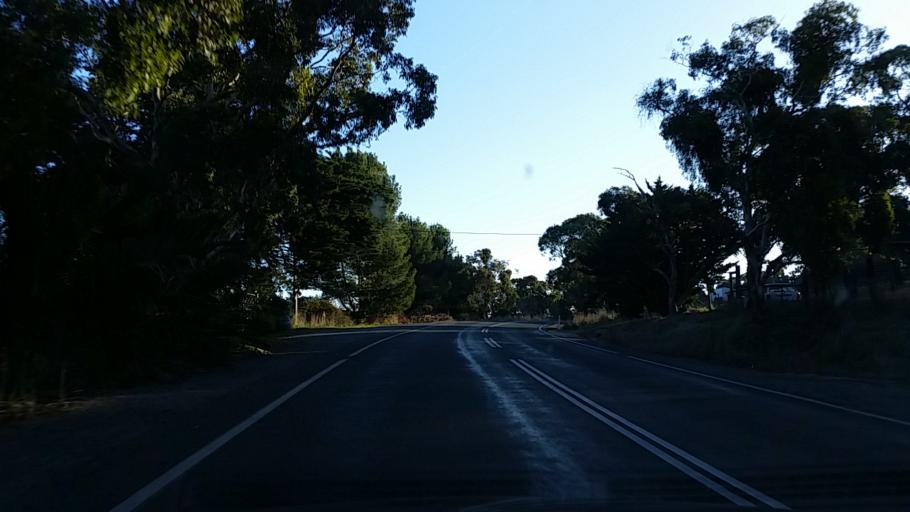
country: AU
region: South Australia
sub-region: Alexandrina
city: Mount Compass
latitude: -35.3479
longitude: 138.6440
